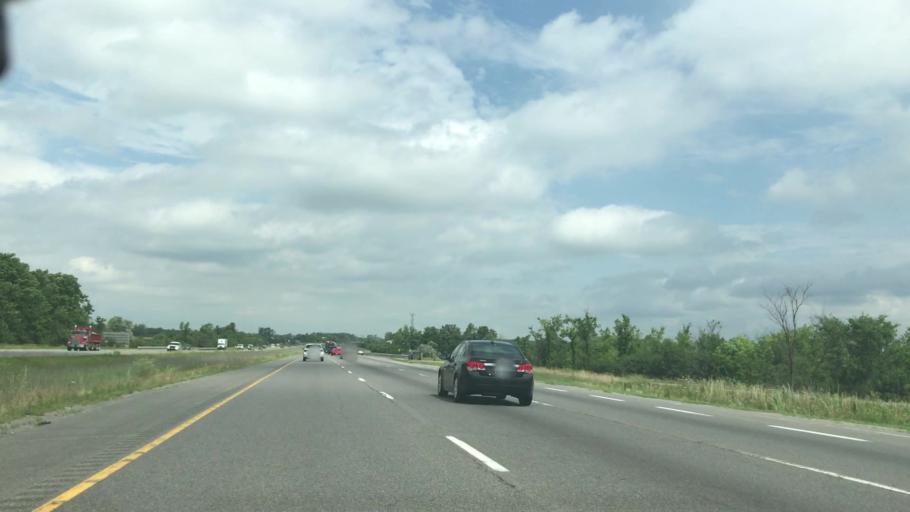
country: CA
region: Ontario
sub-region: York
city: Richmond Hill
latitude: 43.9425
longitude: -79.3901
